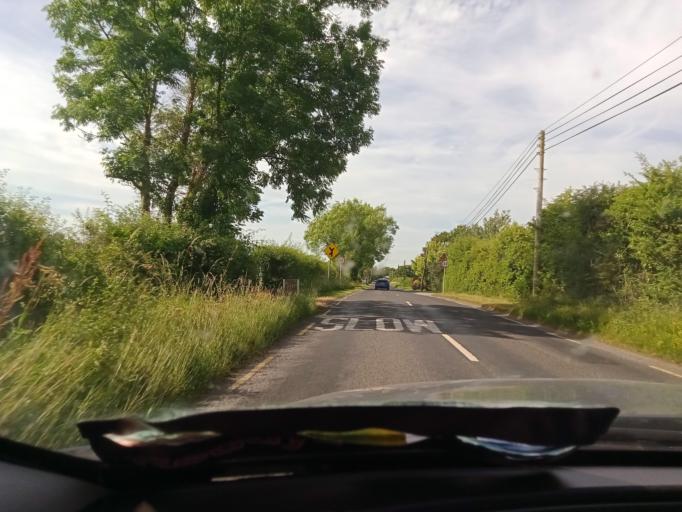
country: IE
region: Leinster
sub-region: Laois
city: Mountmellick
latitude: 53.1051
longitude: -7.3407
